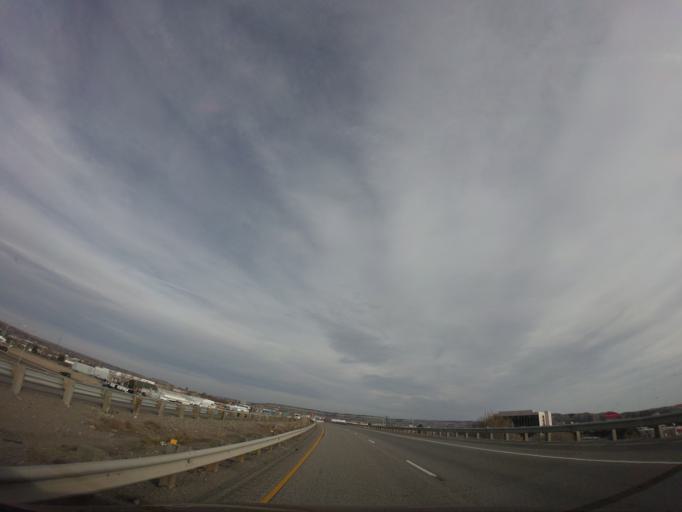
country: US
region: Montana
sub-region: Yellowstone County
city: Billings
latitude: 45.7498
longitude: -108.5559
